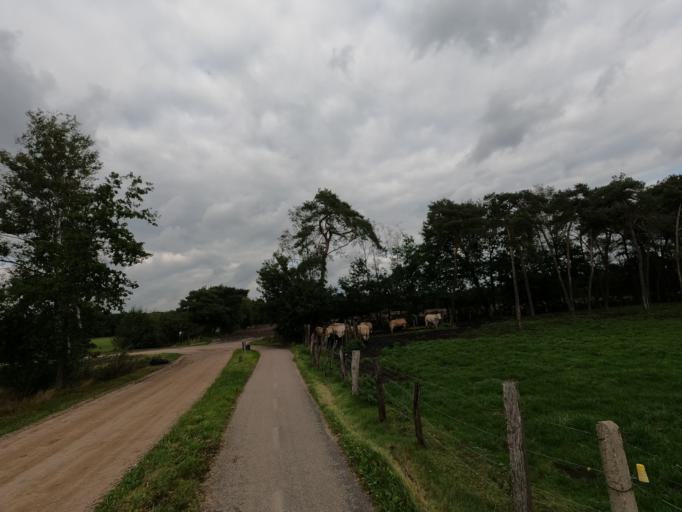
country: BE
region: Flanders
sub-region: Provincie Antwerpen
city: Kasterlee
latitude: 51.2377
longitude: 5.0235
